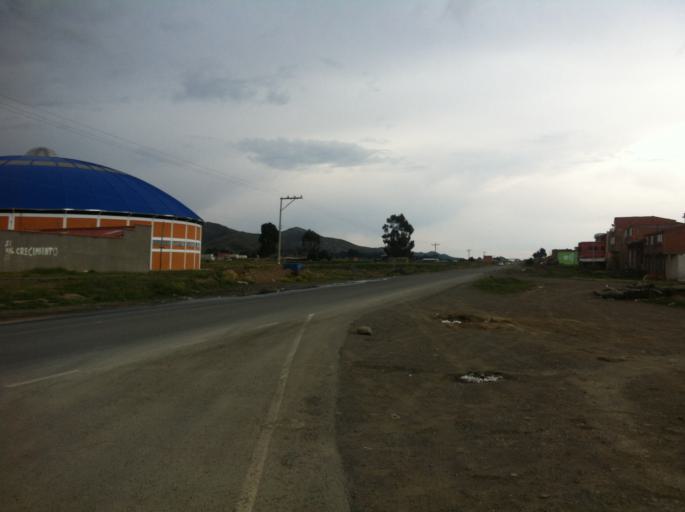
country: BO
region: La Paz
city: Huarina
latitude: -16.2008
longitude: -68.5980
